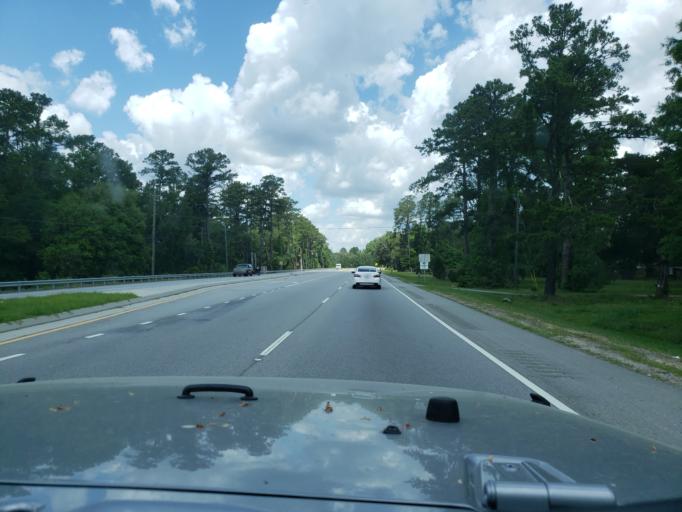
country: US
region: Georgia
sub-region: Chatham County
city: Georgetown
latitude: 32.0435
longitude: -81.2116
